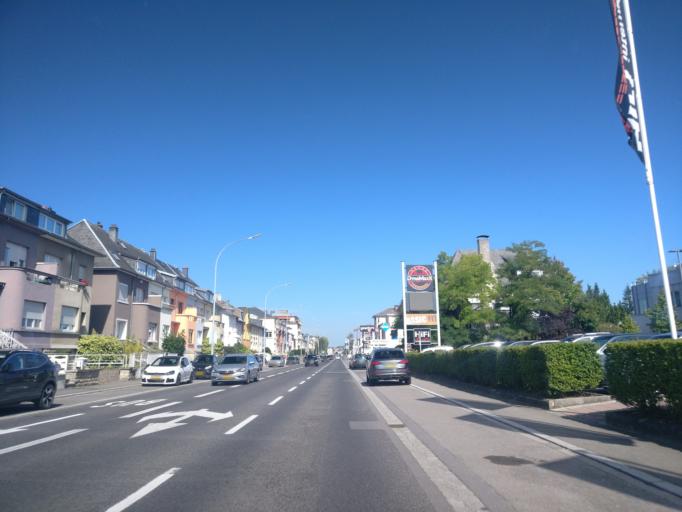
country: LU
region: Luxembourg
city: Bereldange
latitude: 49.6506
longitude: 6.1277
